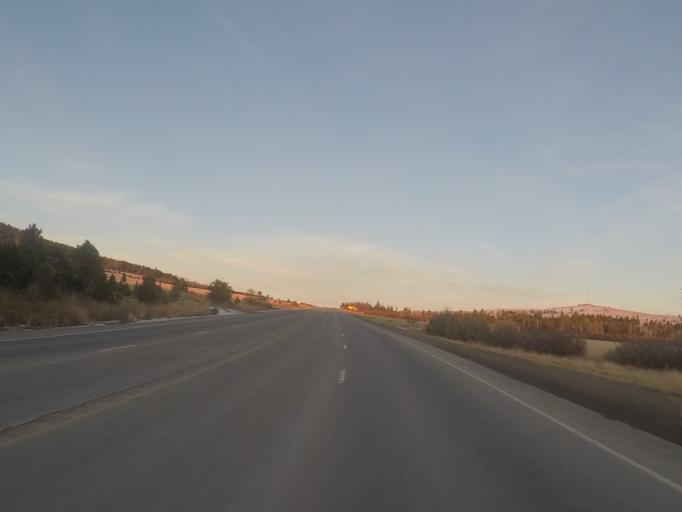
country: US
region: Montana
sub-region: Lewis and Clark County
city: Helena West Side
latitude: 46.5568
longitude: -112.3251
